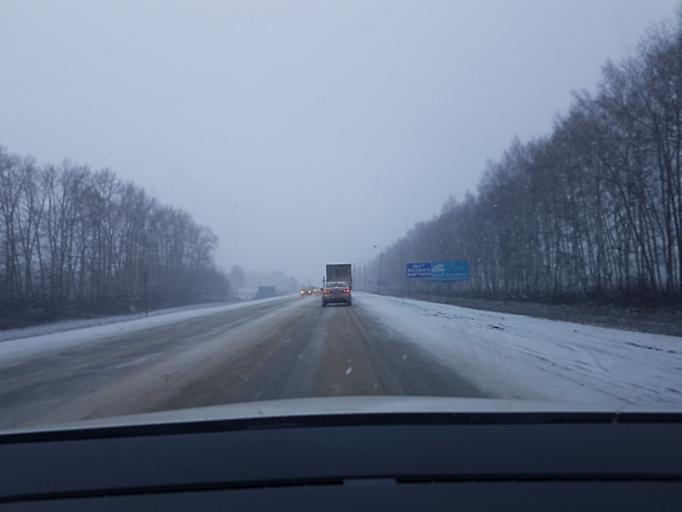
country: RU
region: Tambov
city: Pervomayskiy
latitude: 53.3094
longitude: 40.2204
